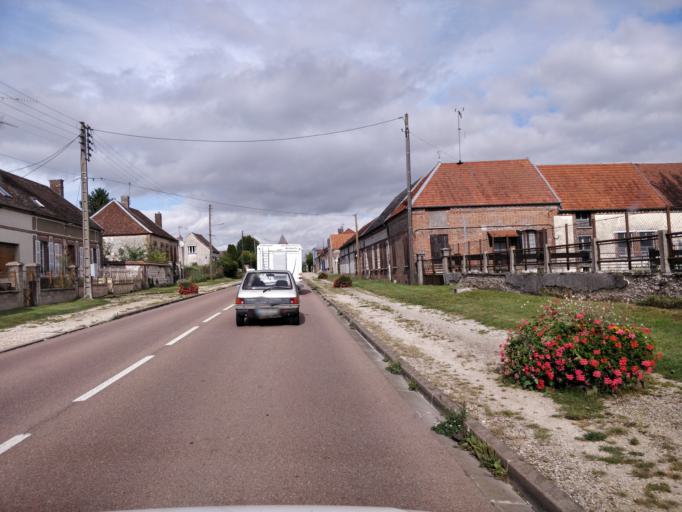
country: FR
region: Champagne-Ardenne
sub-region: Departement de l'Aube
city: Aix-en-Othe
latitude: 48.2546
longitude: 3.7238
